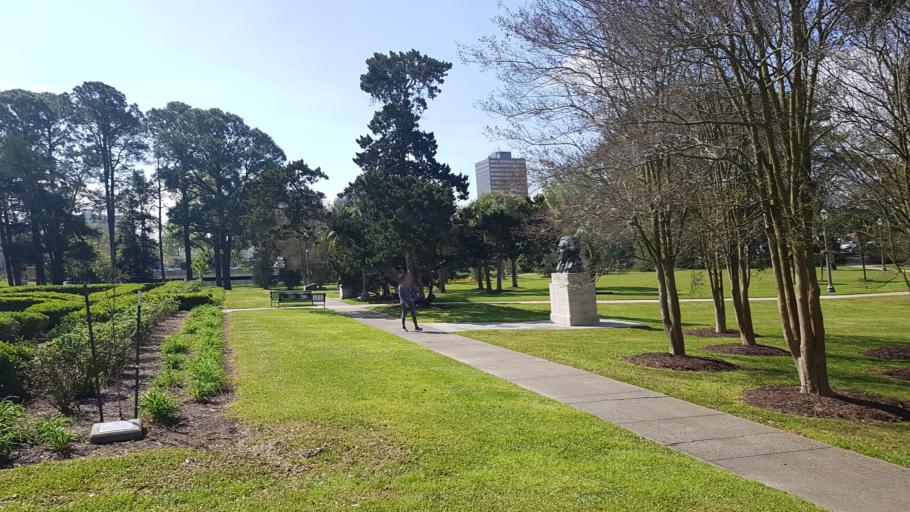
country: US
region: Louisiana
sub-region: West Baton Rouge Parish
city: Port Allen
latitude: 30.4579
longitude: -91.1851
